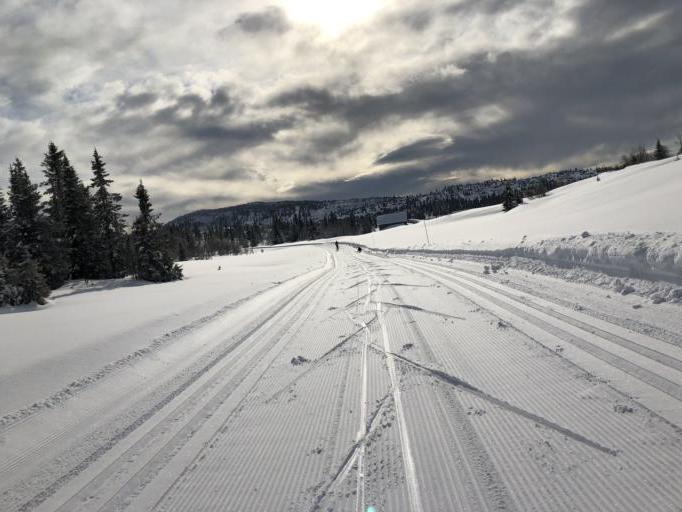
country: NO
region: Oppland
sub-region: Gausdal
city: Segalstad bru
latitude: 61.3176
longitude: 10.0596
